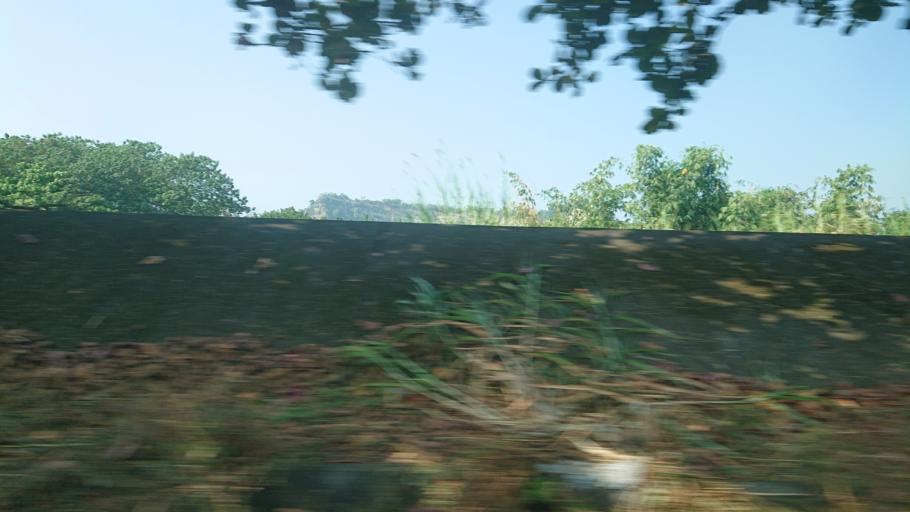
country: TW
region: Taiwan
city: Lugu
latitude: 23.7415
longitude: 120.6582
